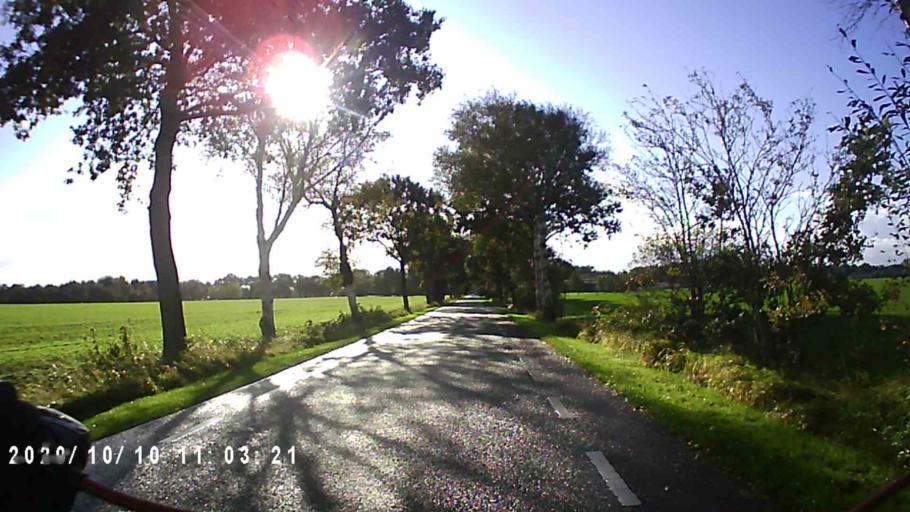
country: NL
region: Friesland
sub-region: Gemeente Achtkarspelen
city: Surhuisterveen
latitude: 53.1347
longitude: 6.2225
